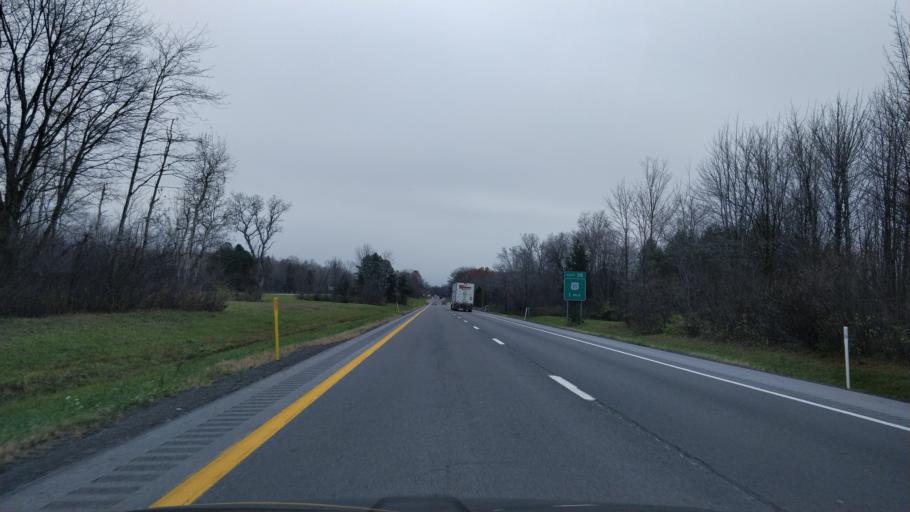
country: US
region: New York
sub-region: Jefferson County
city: Adams
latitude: 43.6943
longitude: -76.0745
